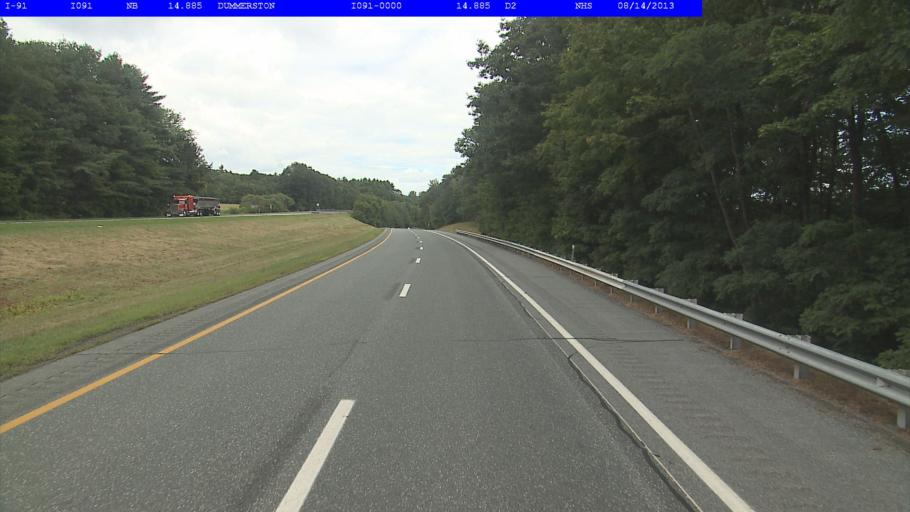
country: US
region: New Hampshire
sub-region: Cheshire County
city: Chesterfield
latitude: 42.9246
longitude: -72.5267
